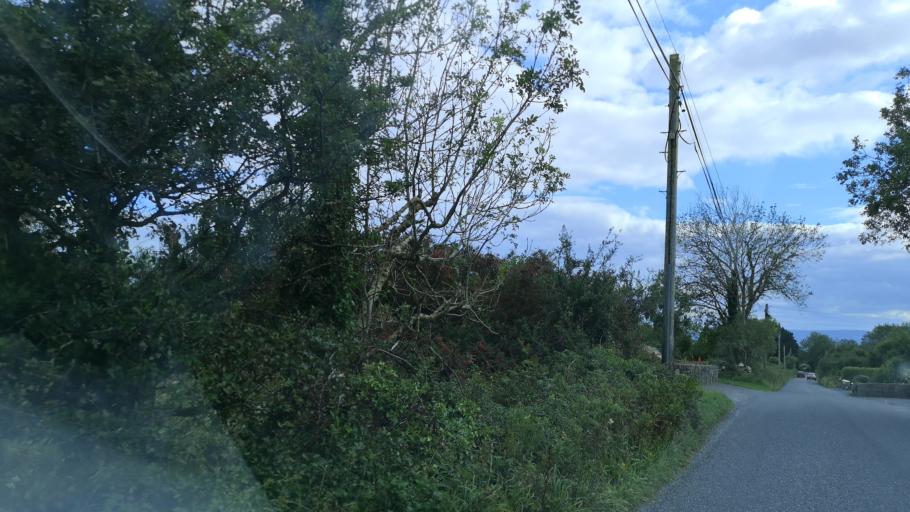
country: IE
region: Connaught
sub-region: County Galway
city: Bearna
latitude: 53.2606
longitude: -9.1525
